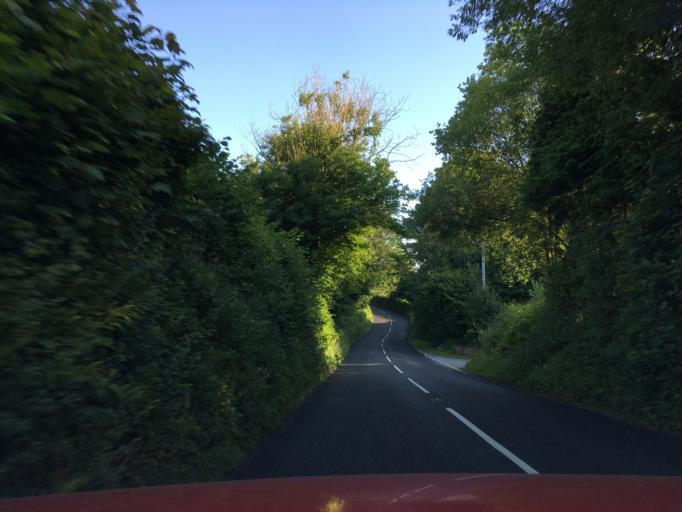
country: GB
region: Wales
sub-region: Monmouthshire
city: Tintern
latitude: 51.7241
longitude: -2.6353
